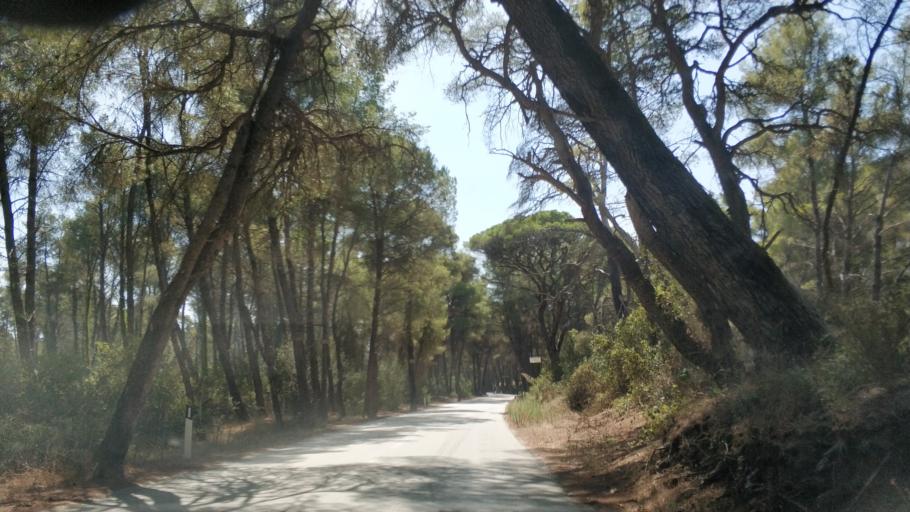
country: AL
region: Fier
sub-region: Rrethi i Lushnjes
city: Divjake
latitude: 40.9786
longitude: 19.4816
